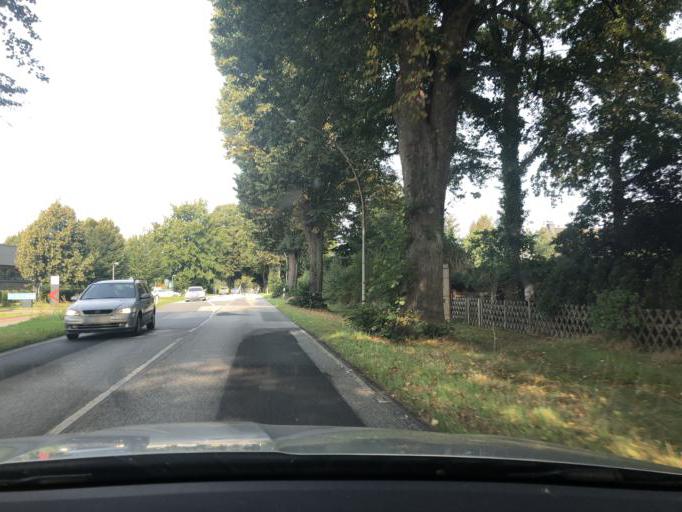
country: DE
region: Schleswig-Holstein
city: Gross Gronau
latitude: 53.8138
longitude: 10.7403
